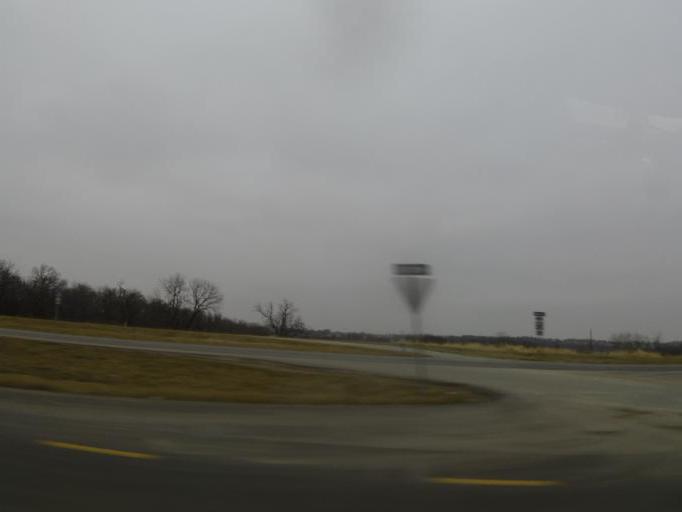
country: US
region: Missouri
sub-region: Marion County
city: Hannibal
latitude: 39.7439
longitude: -91.4419
